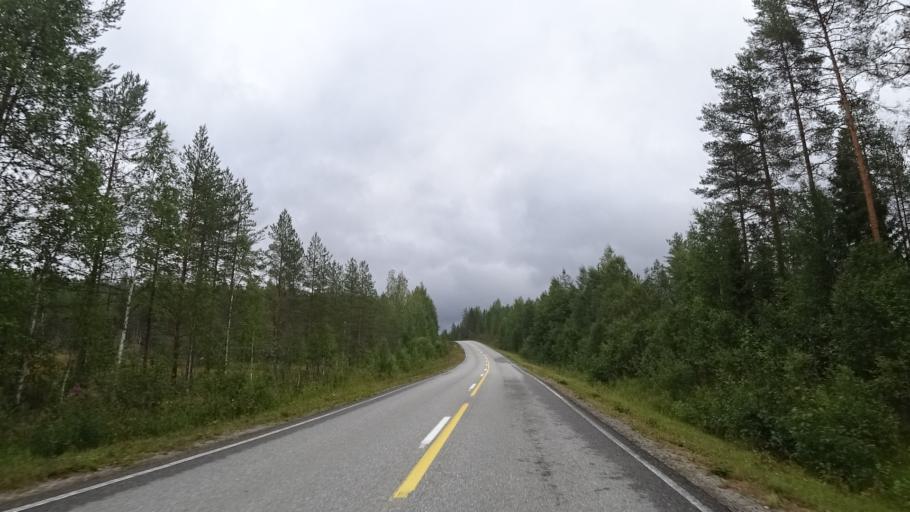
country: FI
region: North Karelia
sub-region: Joensuu
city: Ilomantsi
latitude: 63.2510
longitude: 30.7254
